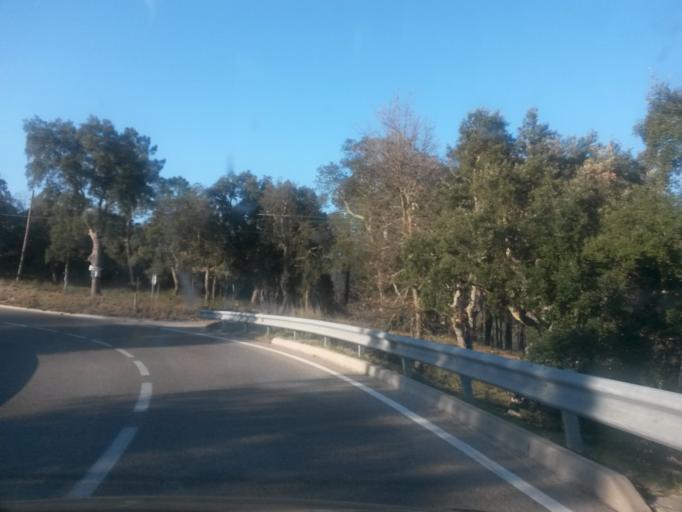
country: ES
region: Catalonia
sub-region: Provincia de Girona
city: Darnius
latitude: 42.3686
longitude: 2.8232
